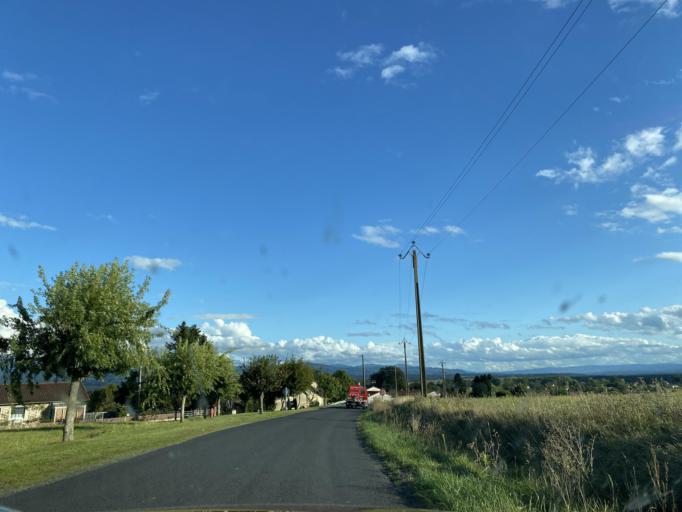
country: FR
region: Auvergne
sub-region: Departement du Puy-de-Dome
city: Saint-Sylvestre-Pragoulin
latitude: 46.0034
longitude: 3.4133
